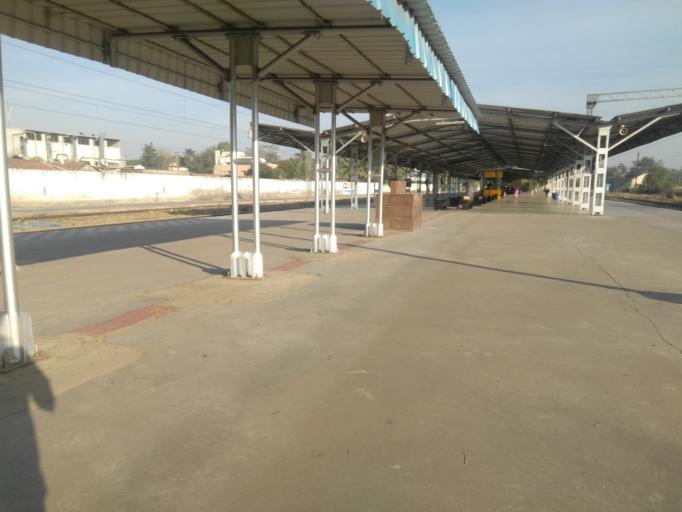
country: IN
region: Tamil Nadu
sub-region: Coimbatore
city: Coimbatore
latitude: 11.0188
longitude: 76.9552
